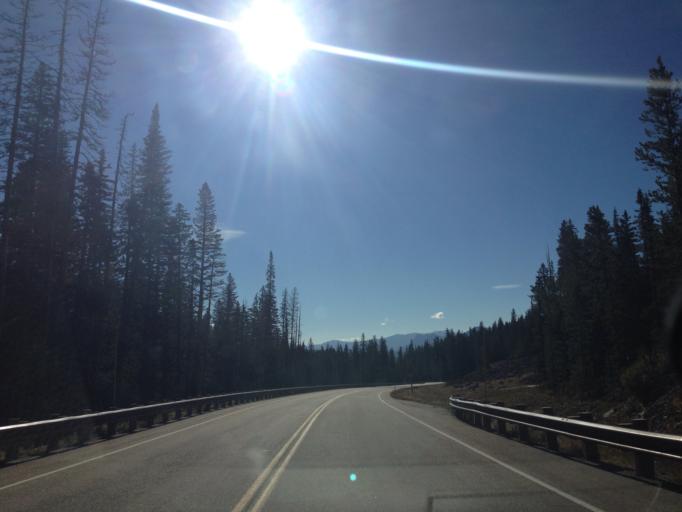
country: US
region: Montana
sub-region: Carbon County
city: Red Lodge
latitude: 45.0107
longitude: -109.8667
